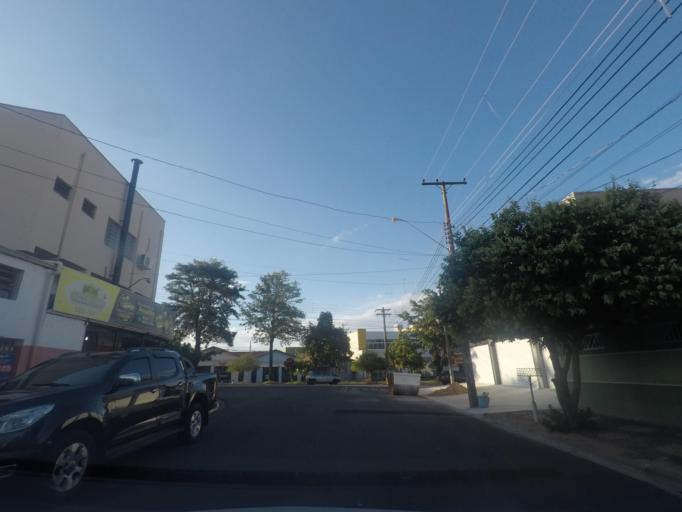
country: BR
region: Sao Paulo
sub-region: Sumare
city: Sumare
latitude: -22.8135
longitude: -47.2842
